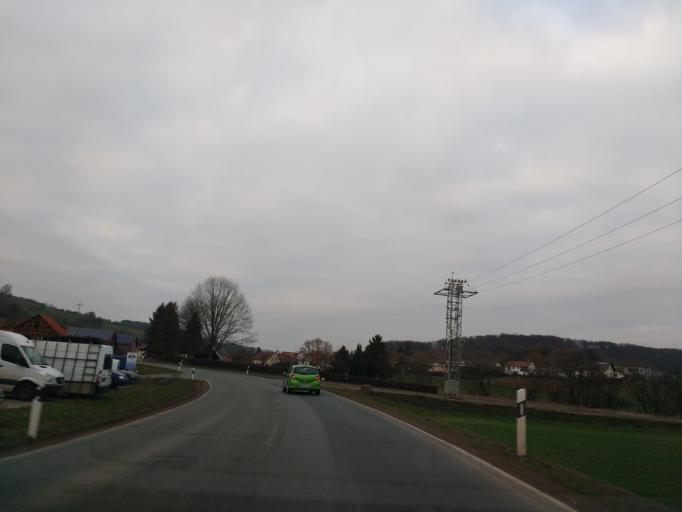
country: DE
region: Hesse
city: Bebra
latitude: 51.0160
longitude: 9.7756
